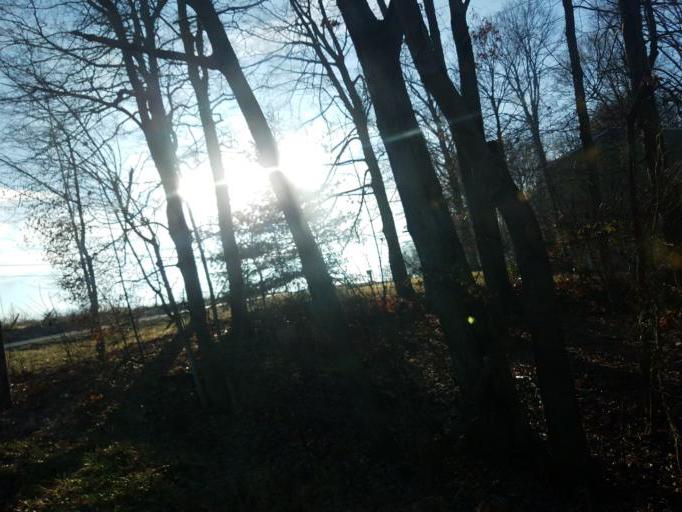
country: US
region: Ohio
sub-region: Knox County
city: Gambier
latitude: 40.3992
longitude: -82.4101
